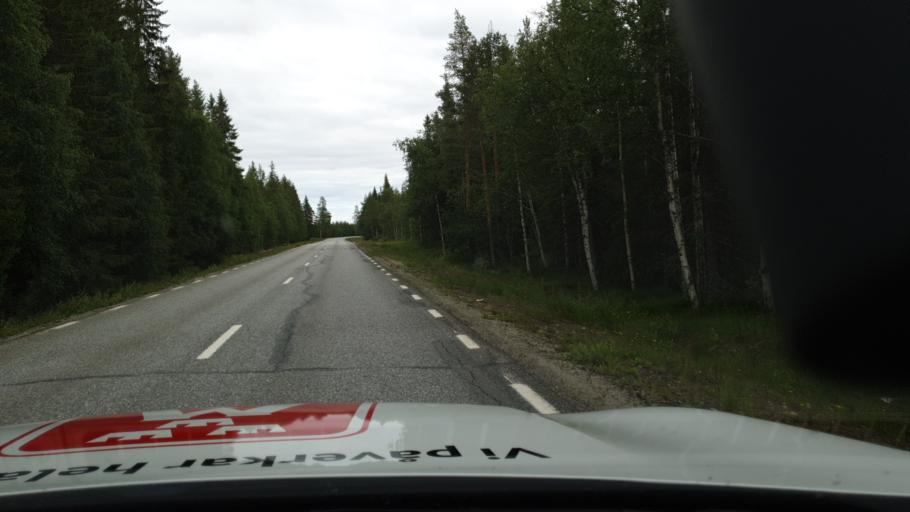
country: SE
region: Vaesterbotten
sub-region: Lycksele Kommun
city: Soderfors
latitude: 64.6334
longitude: 17.9678
